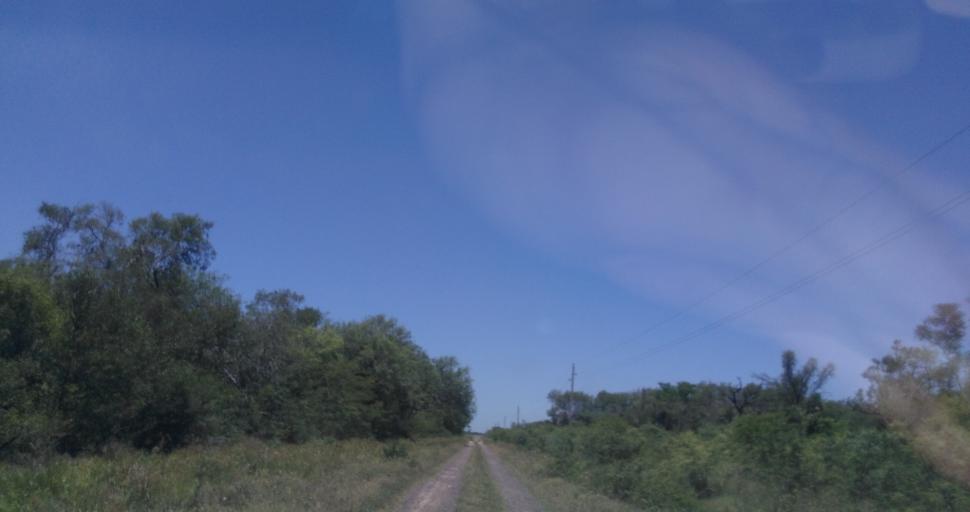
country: AR
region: Chaco
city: Fontana
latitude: -27.4801
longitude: -59.0686
